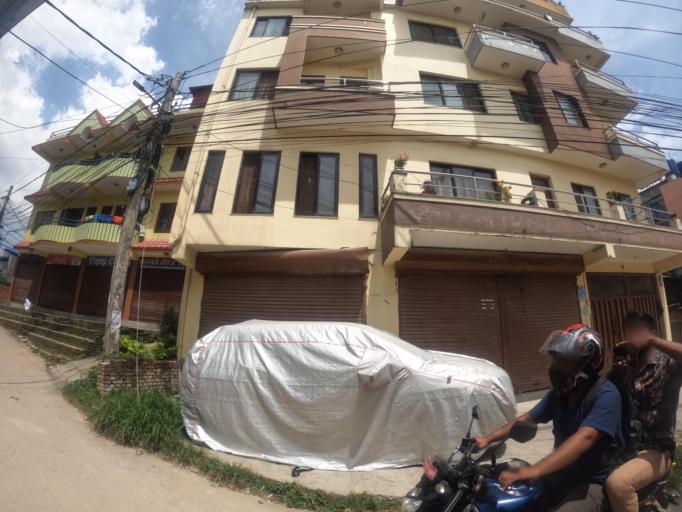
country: NP
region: Central Region
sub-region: Bagmati Zone
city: Patan
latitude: 27.6752
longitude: 85.3668
